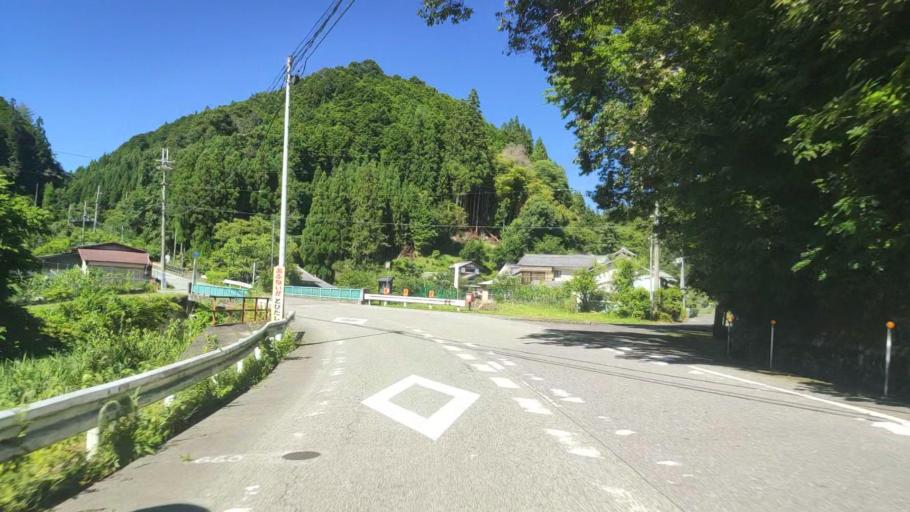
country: JP
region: Nara
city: Yoshino-cho
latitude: 34.4122
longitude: 135.9344
